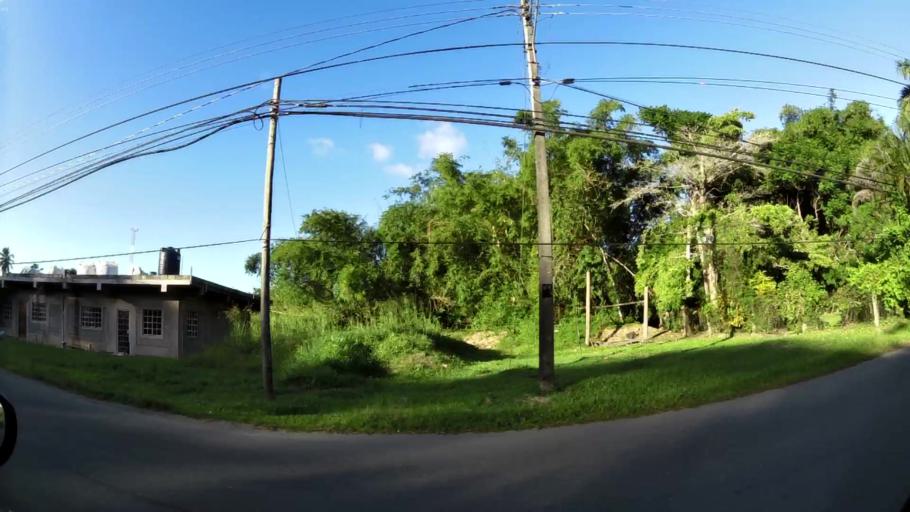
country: TT
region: Tobago
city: Scarborough
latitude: 11.2159
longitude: -60.7723
